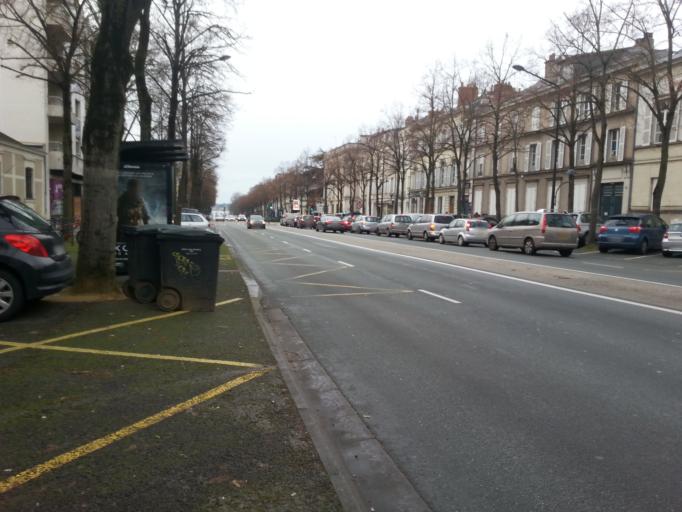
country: FR
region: Pays de la Loire
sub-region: Departement de Maine-et-Loire
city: Angers
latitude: 47.4669
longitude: -0.5544
